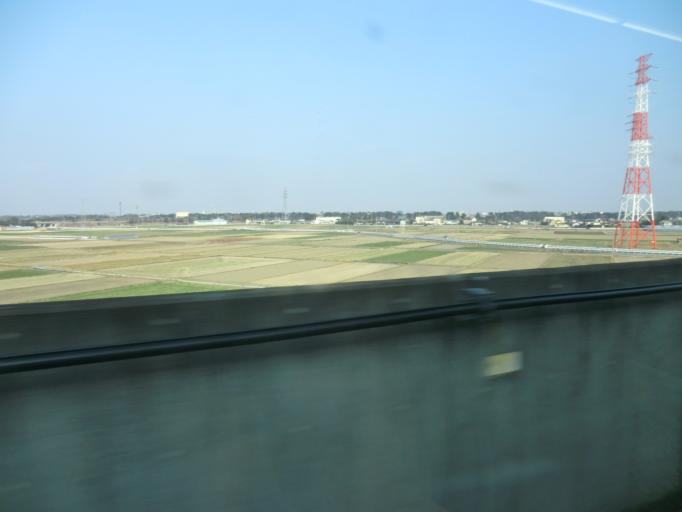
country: JP
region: Gunma
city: Fujioka
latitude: 36.2671
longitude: 139.0874
